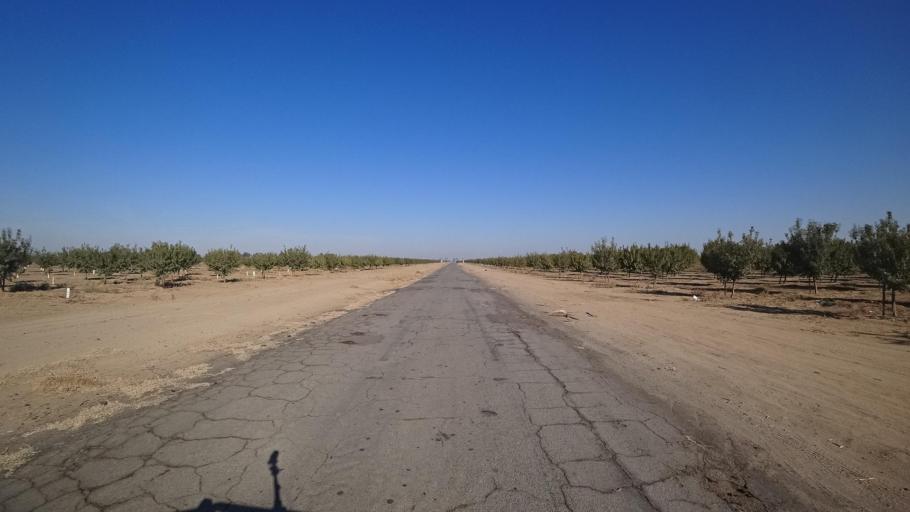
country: US
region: California
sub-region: Kern County
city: Delano
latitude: 35.7474
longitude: -119.2319
